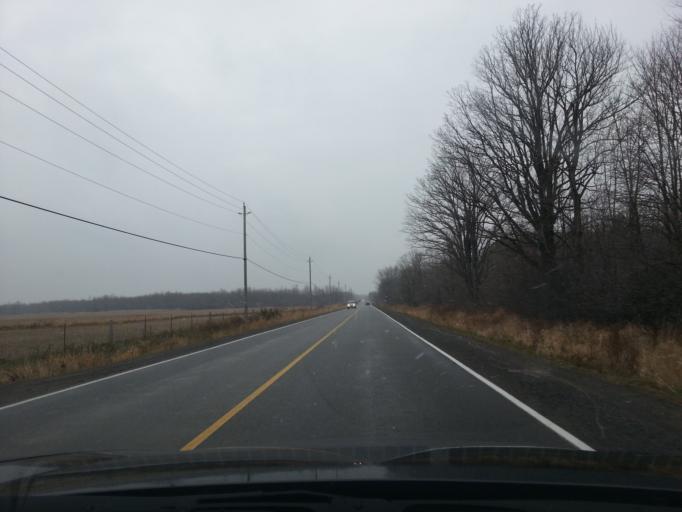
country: CA
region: Ontario
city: Carleton Place
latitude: 45.1490
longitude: -76.1055
